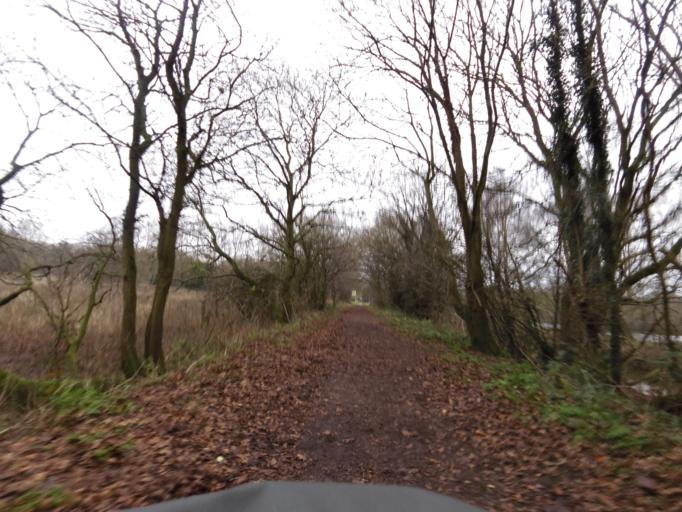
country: GB
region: England
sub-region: Norfolk
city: Mattishall
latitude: 52.7245
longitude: 1.1121
